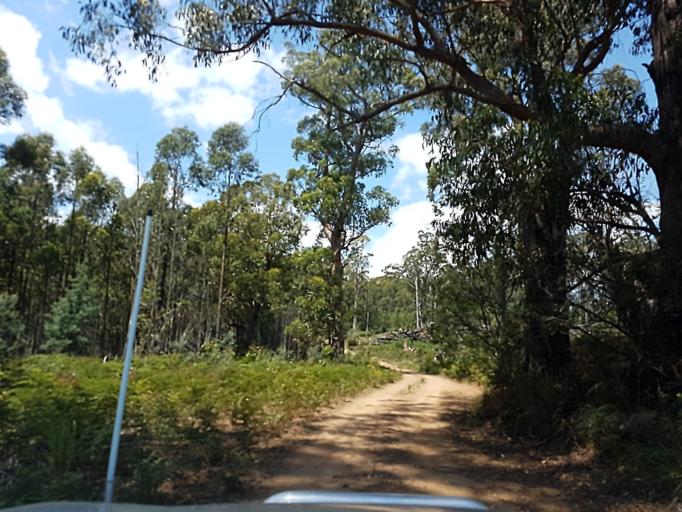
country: AU
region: Victoria
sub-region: East Gippsland
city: Lakes Entrance
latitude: -37.3868
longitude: 148.2878
